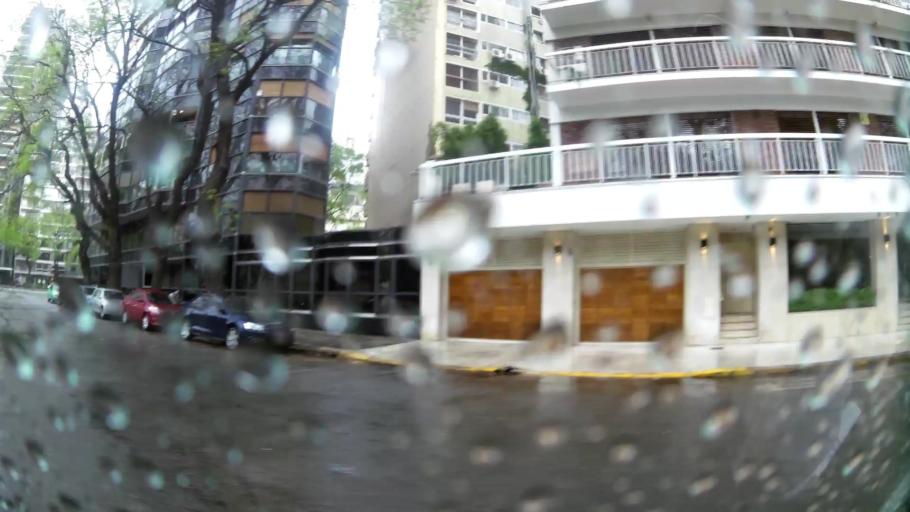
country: AR
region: Buenos Aires F.D.
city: Retiro
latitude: -34.5808
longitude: -58.4030
